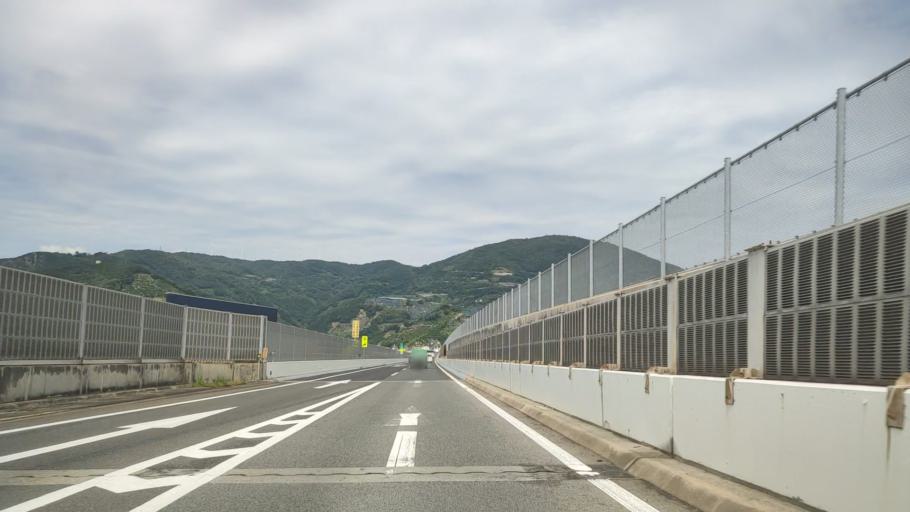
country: JP
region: Wakayama
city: Kainan
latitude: 34.0642
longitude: 135.2002
